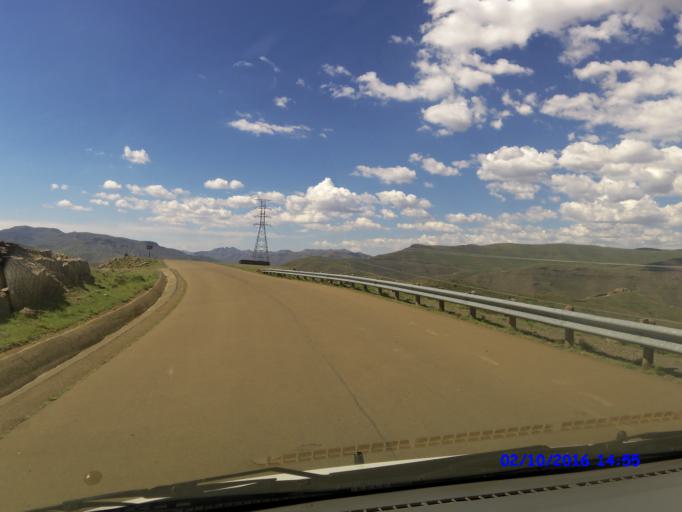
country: LS
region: Maseru
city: Nako
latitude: -29.4713
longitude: 28.0893
